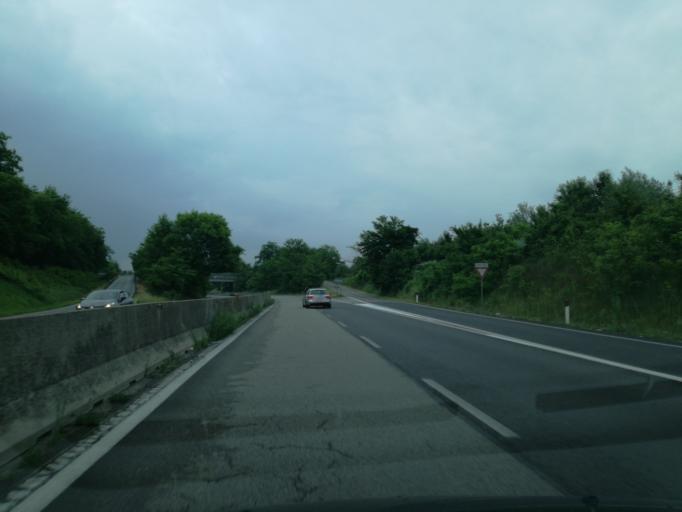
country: IT
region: Lombardy
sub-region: Provincia di Monza e Brianza
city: Villasanta
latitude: 45.5963
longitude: 9.3141
